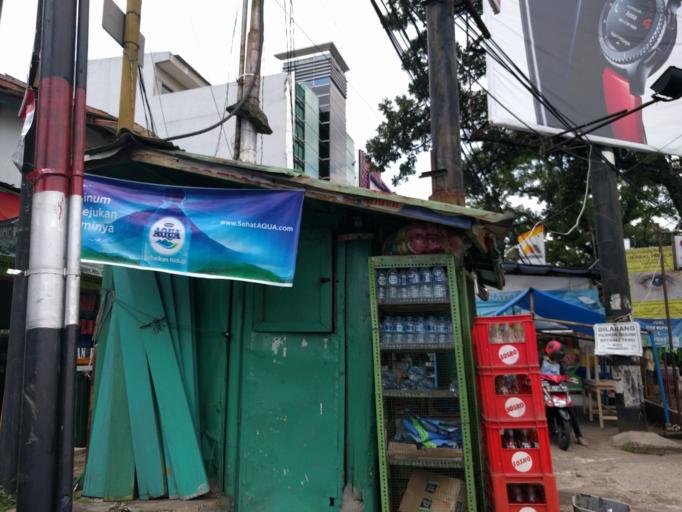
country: ID
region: West Java
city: Bogor
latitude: -6.5690
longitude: 106.8092
